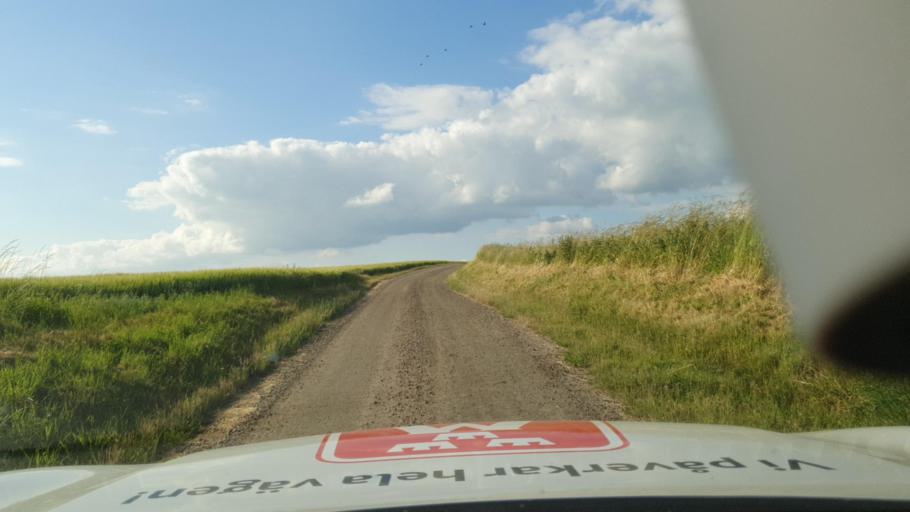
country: SE
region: Skane
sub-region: Skurups Kommun
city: Rydsgard
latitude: 55.4918
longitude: 13.5757
